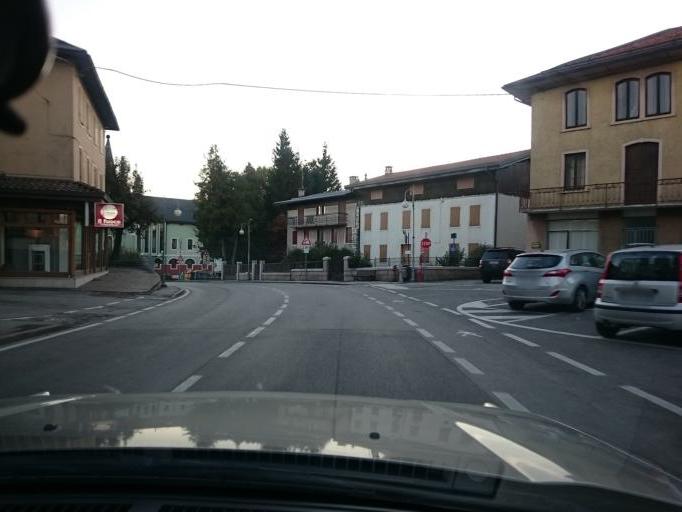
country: IT
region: Veneto
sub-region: Provincia di Vicenza
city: Canove di Roana
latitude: 45.8640
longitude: 11.4734
